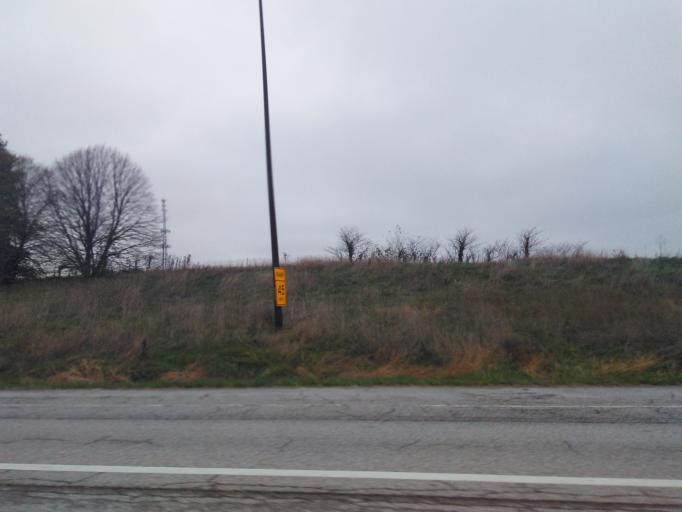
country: US
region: Illinois
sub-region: Bond County
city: Greenville
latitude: 38.8331
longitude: -89.5416
